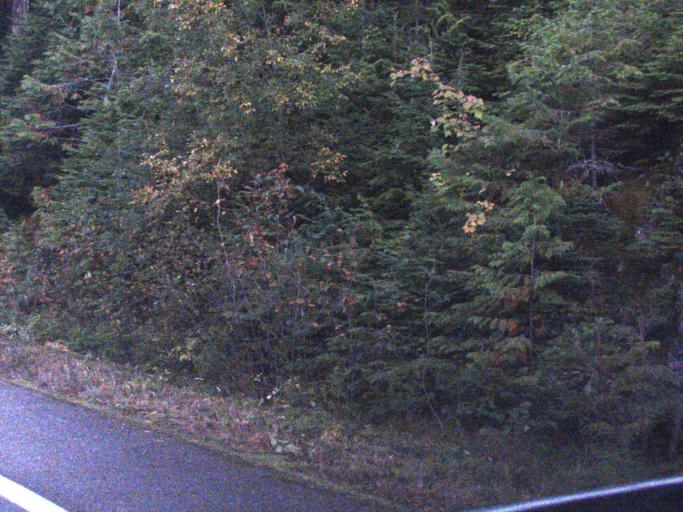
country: US
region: Washington
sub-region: Snohomish County
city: Darrington
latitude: 48.7250
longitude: -121.0307
